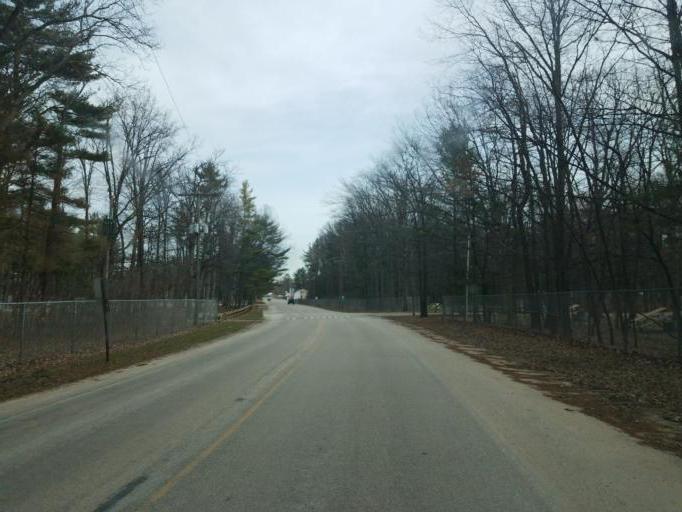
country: US
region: Michigan
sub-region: Oceana County
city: Hart
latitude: 43.6617
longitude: -86.4951
